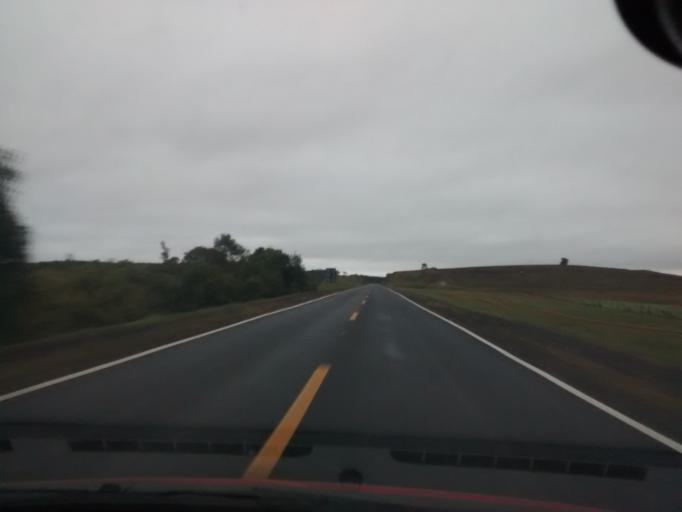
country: BR
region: Rio Grande do Sul
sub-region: Vacaria
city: Estrela
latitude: -28.1593
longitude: -50.6660
